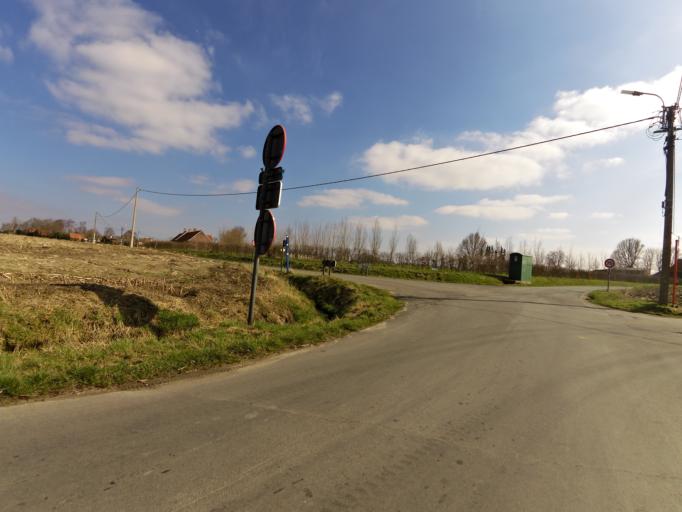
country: BE
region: Flanders
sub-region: Provincie West-Vlaanderen
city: Torhout
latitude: 51.0530
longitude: 3.0960
